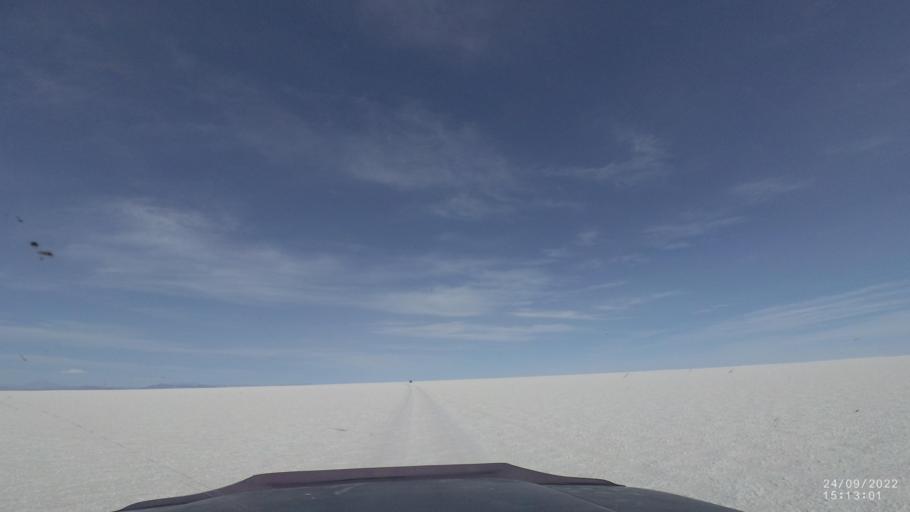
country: BO
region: Potosi
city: Colchani
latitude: -19.9542
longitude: -67.4675
